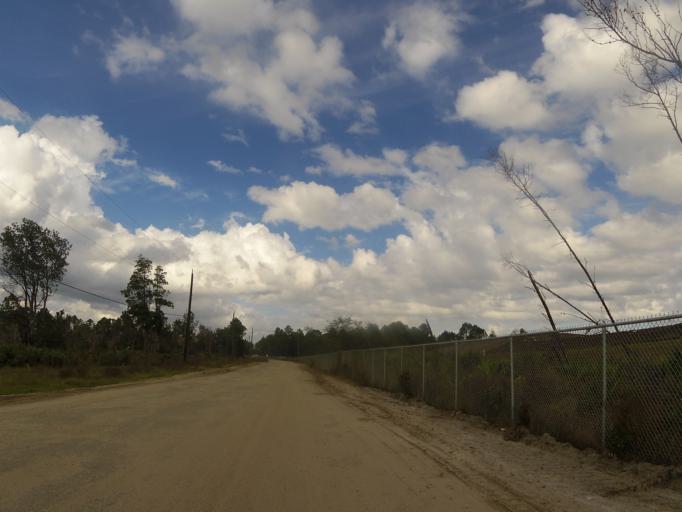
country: US
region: Florida
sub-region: Saint Johns County
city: Villano Beach
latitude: 29.9871
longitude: -81.3878
